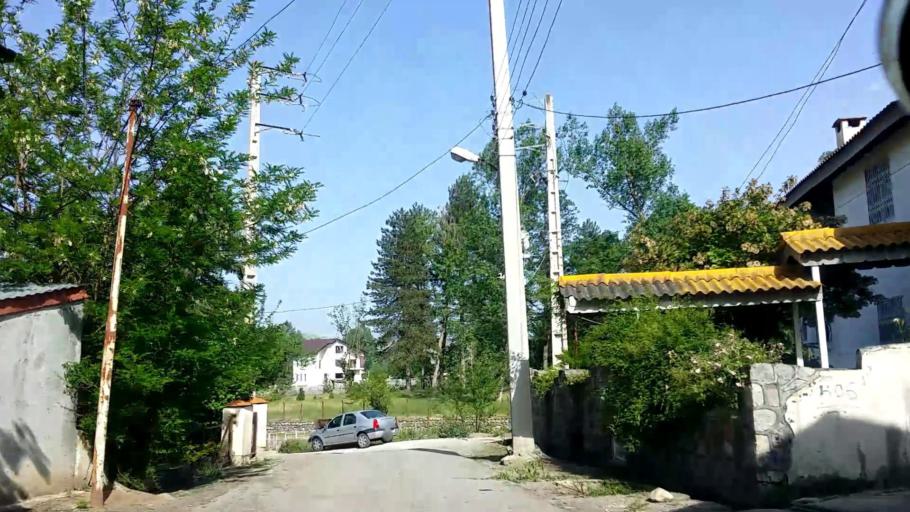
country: IR
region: Mazandaran
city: `Abbasabad
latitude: 36.5274
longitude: 51.1822
